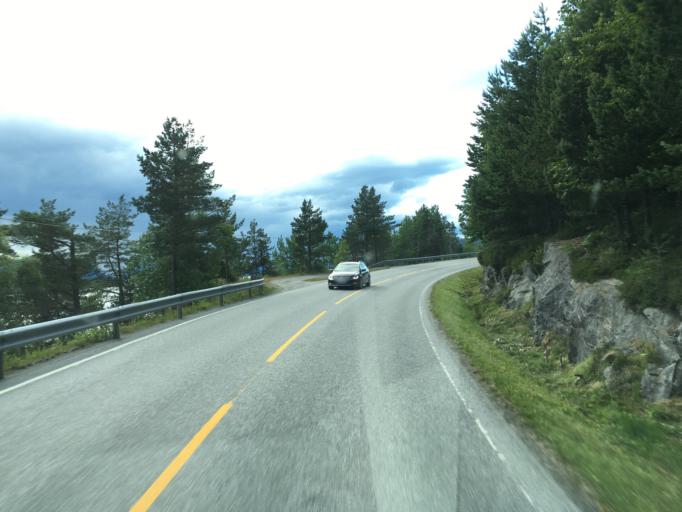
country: NO
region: More og Romsdal
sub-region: Tingvoll
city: Tingvoll
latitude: 62.9740
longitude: 8.0547
